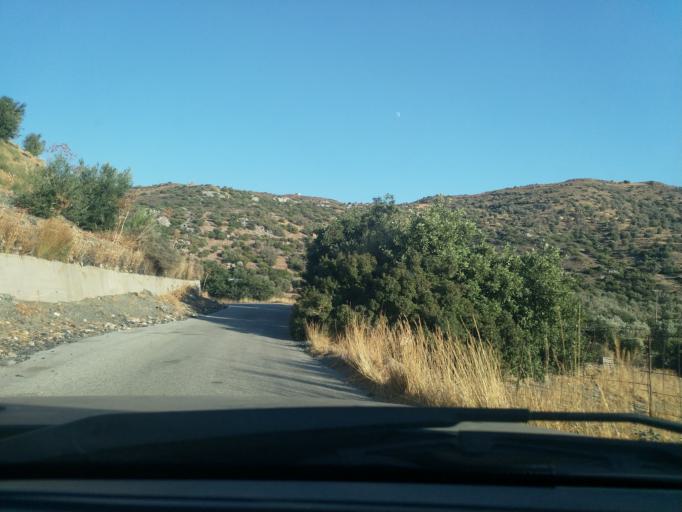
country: GR
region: Crete
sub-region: Nomos Rethymnis
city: Agia Galini
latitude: 35.1162
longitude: 24.5645
